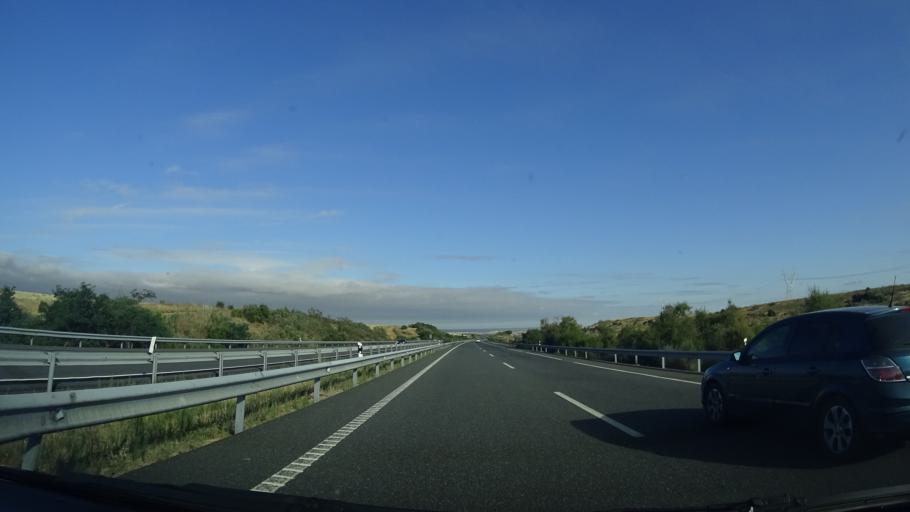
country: ES
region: Castille and Leon
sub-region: Provincia de Segovia
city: Labajos
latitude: 40.8271
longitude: -4.5190
